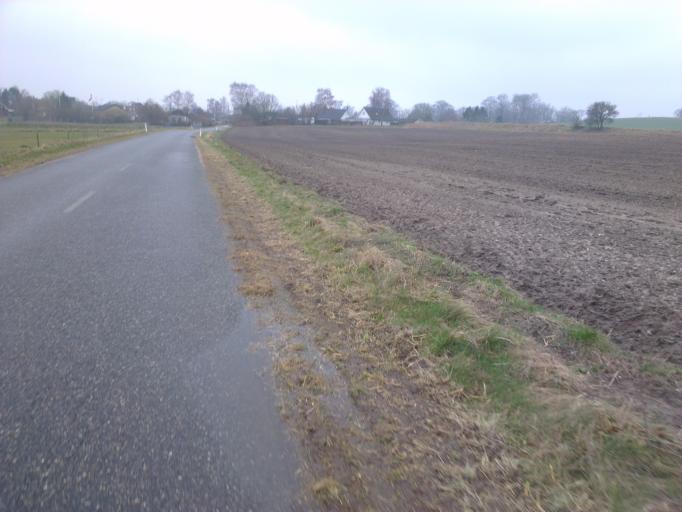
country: DK
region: Capital Region
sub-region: Frederikssund Kommune
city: Skibby
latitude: 55.7974
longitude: 11.9247
